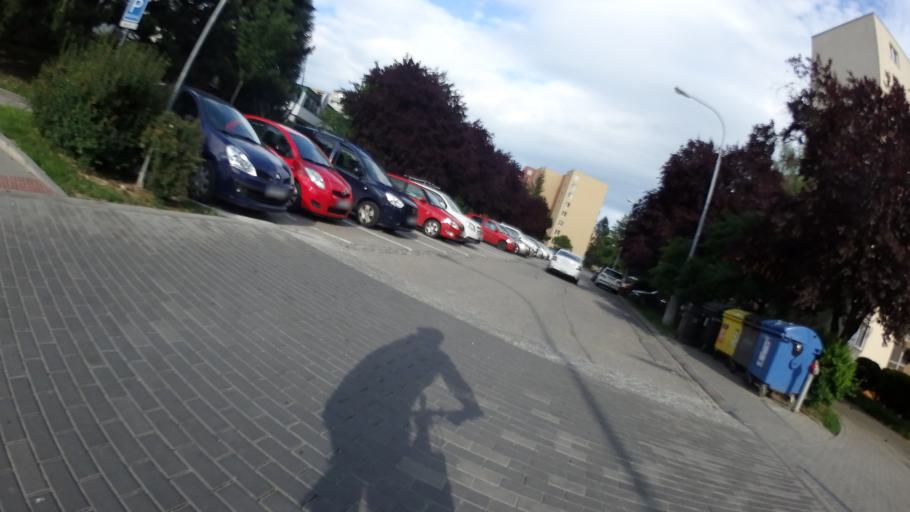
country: CZ
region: South Moravian
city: Moravany
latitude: 49.1696
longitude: 16.5806
